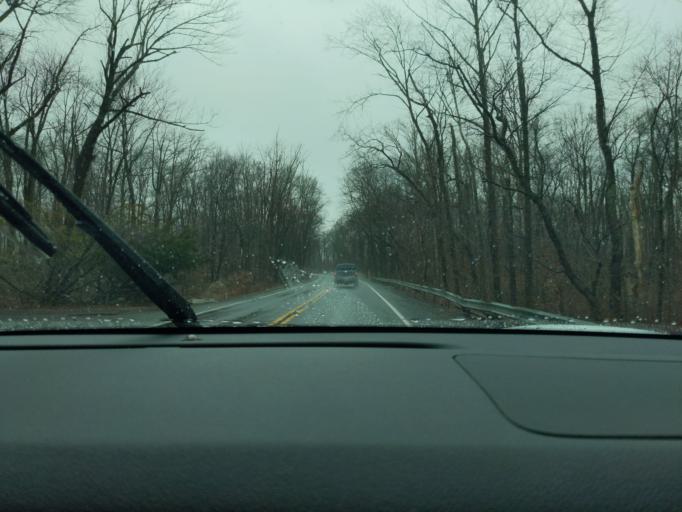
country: US
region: Pennsylvania
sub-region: Bucks County
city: Perkasie
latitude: 40.4245
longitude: -75.2813
